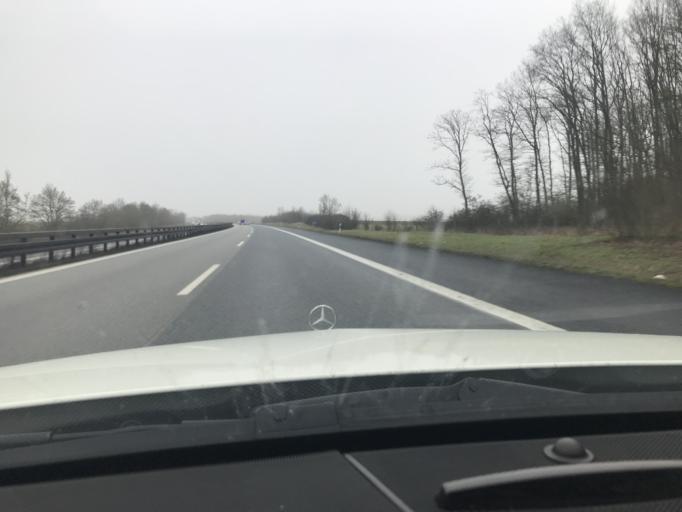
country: DE
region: Bavaria
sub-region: Regierungsbezirk Unterfranken
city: Werneck
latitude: 50.0229
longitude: 10.0689
